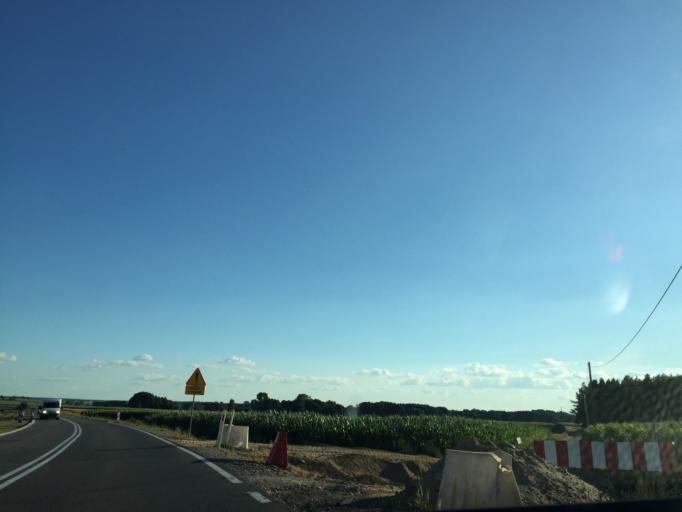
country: PL
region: Podlasie
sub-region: Powiat kolnenski
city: Stawiski
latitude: 53.4309
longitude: 22.1681
